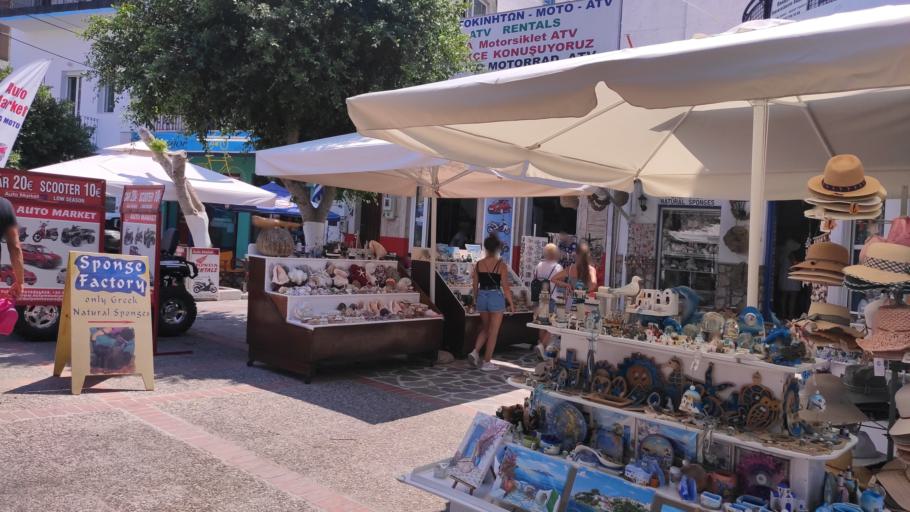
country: GR
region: South Aegean
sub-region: Nomos Dodekanisou
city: Kalymnos
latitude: 36.9466
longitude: 26.9839
